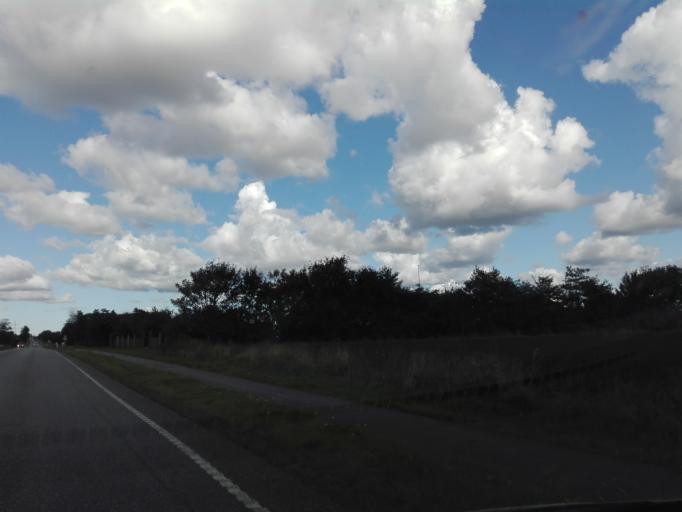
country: DK
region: North Denmark
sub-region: Mariagerfjord Kommune
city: Hobro
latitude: 56.6119
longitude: 9.8067
